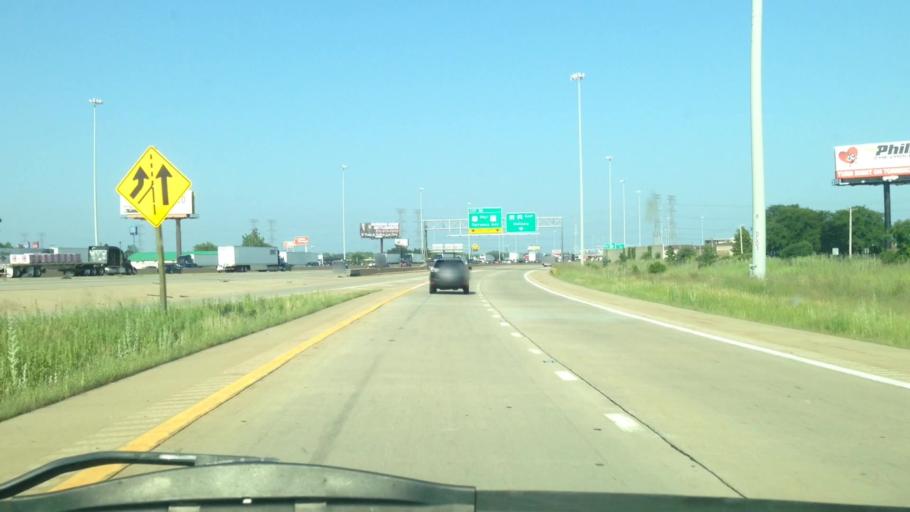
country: US
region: Illinois
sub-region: Cook County
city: Lansing
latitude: 41.5770
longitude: -87.5703
